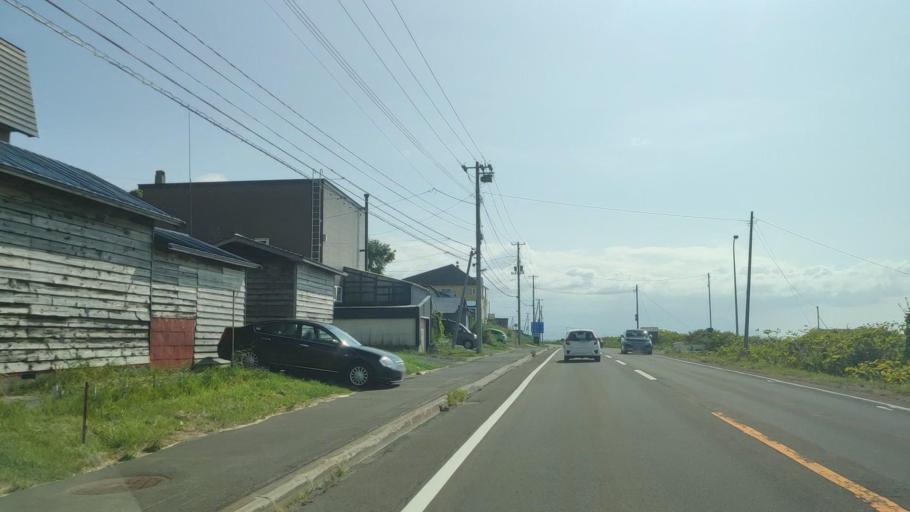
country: JP
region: Hokkaido
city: Rumoi
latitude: 43.9163
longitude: 141.6195
